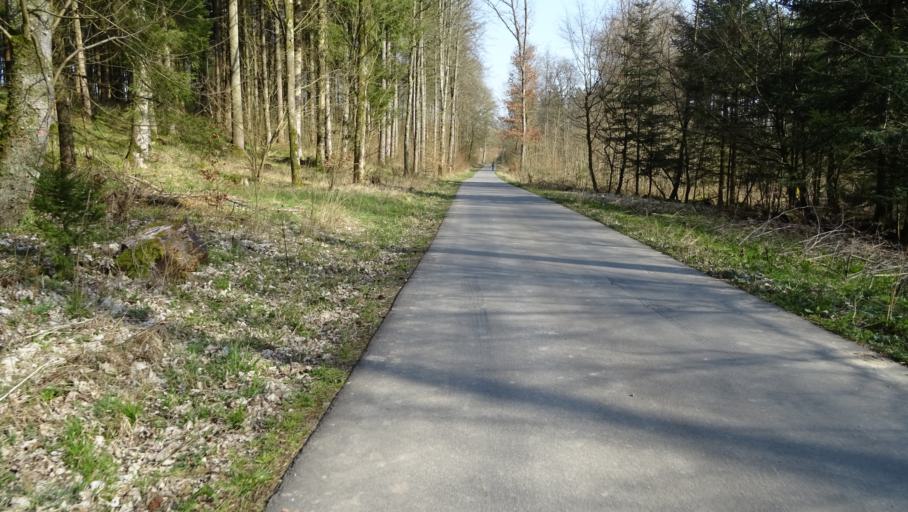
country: DE
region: Baden-Wuerttemberg
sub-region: Regierungsbezirk Stuttgart
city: Roigheim
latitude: 49.3872
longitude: 9.3390
